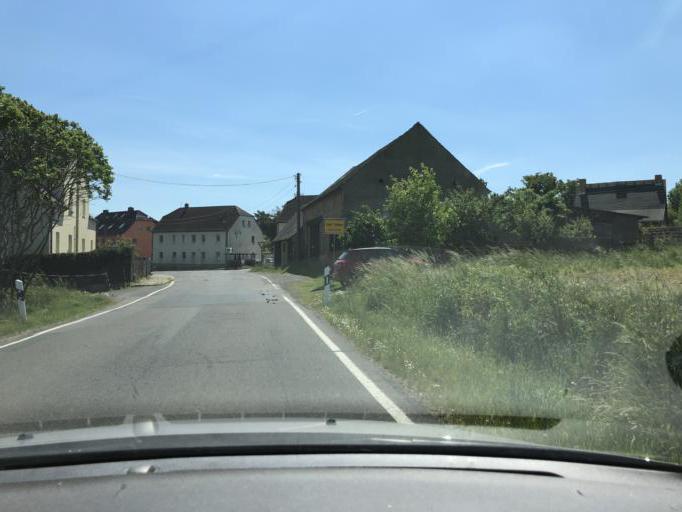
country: DE
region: Saxony
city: Trebsen
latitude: 51.2889
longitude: 12.7467
